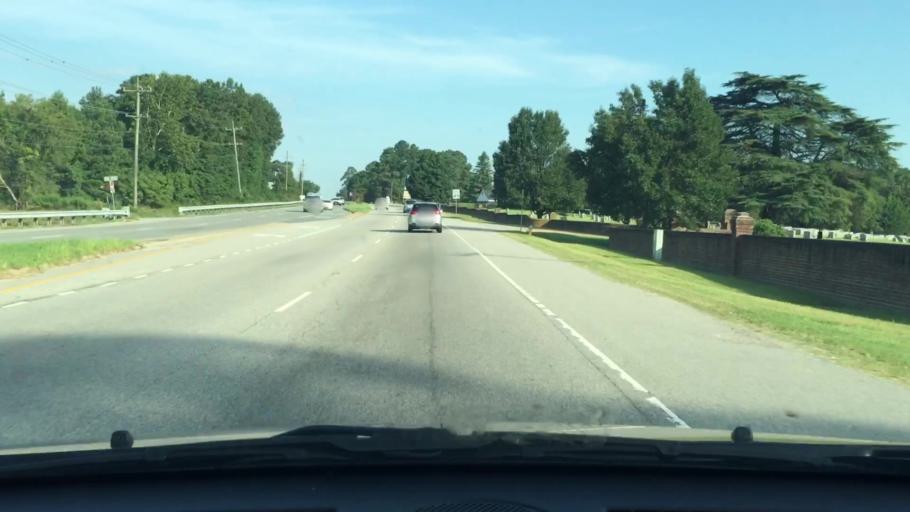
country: US
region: Virginia
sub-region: Isle of Wight County
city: Carrollton
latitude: 36.9399
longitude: -76.5877
